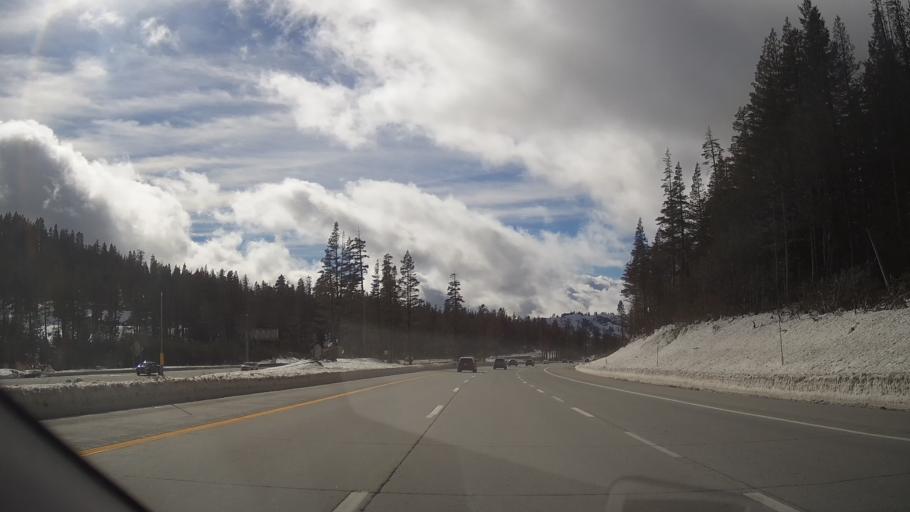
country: US
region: California
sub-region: Nevada County
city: Truckee
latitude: 39.3360
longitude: -120.3547
